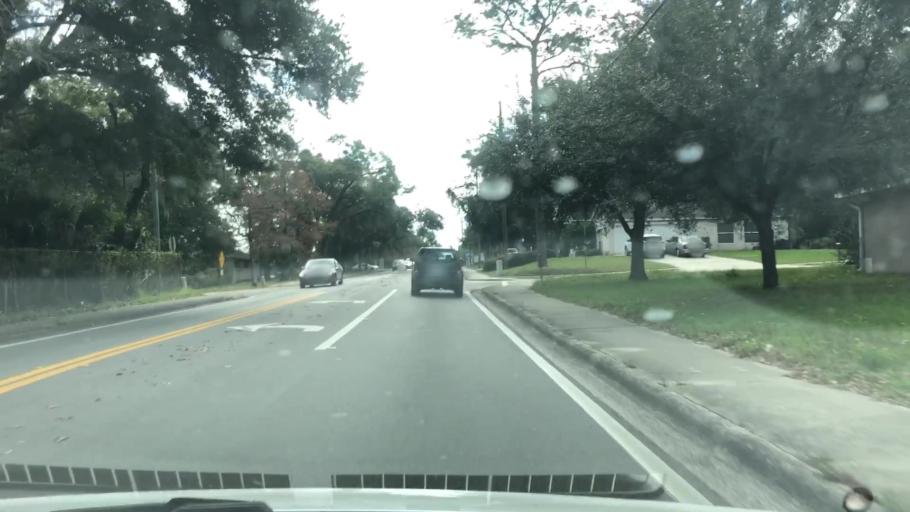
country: US
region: Florida
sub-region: Seminole County
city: Altamonte Springs
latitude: 28.6768
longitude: -81.3739
